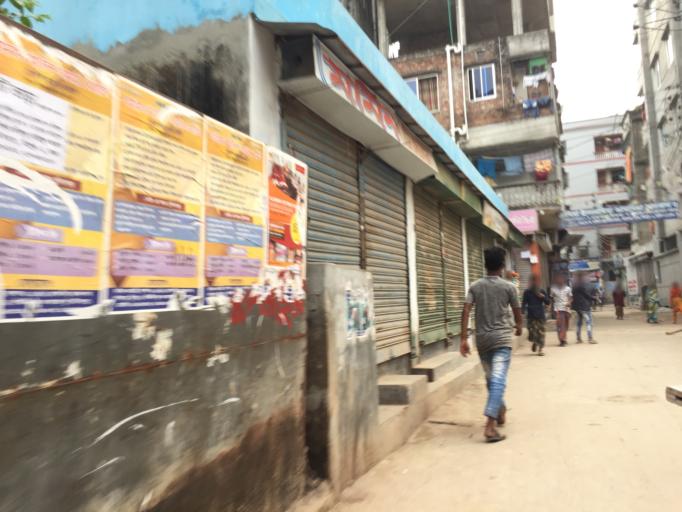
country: BD
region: Dhaka
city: Azimpur
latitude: 23.7934
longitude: 90.3621
